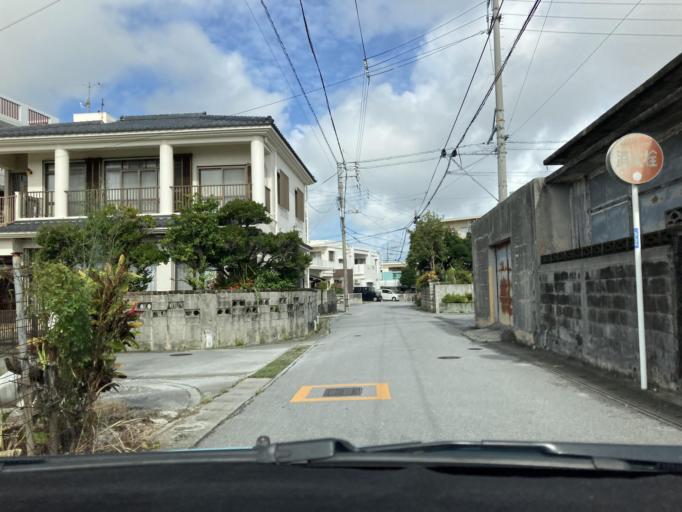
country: JP
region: Okinawa
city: Naha-shi
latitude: 26.2029
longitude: 127.7292
